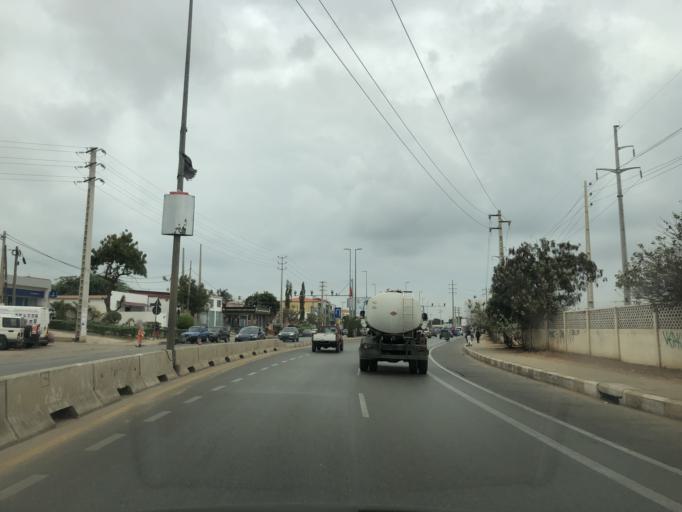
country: AO
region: Luanda
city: Luanda
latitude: -8.8948
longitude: 13.1916
